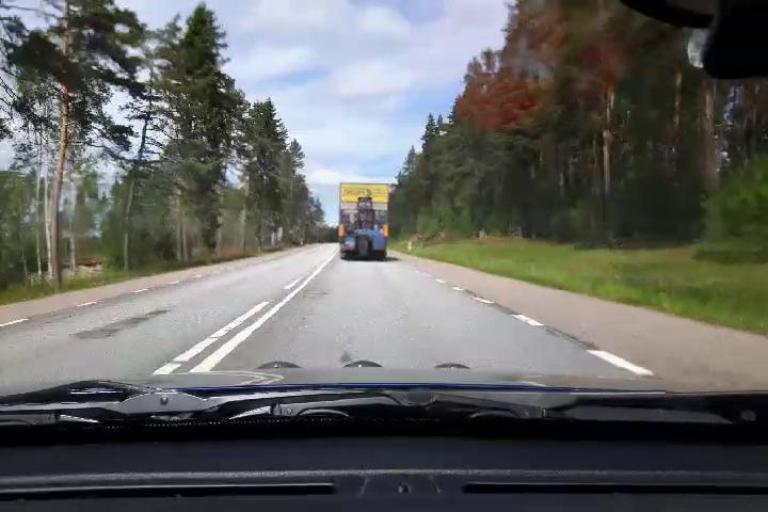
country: SE
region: Uppsala
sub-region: Tierps Kommun
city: Tierp
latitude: 60.2064
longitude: 17.4825
